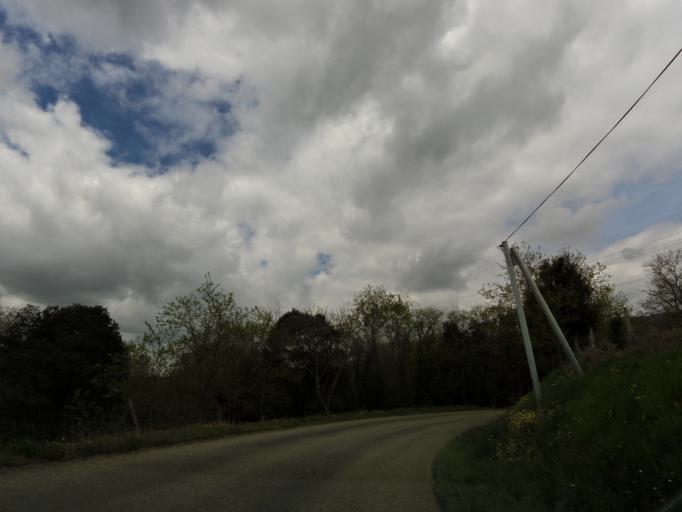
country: FR
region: Languedoc-Roussillon
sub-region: Departement de l'Aude
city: Villepinte
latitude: 43.3507
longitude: 2.0873
